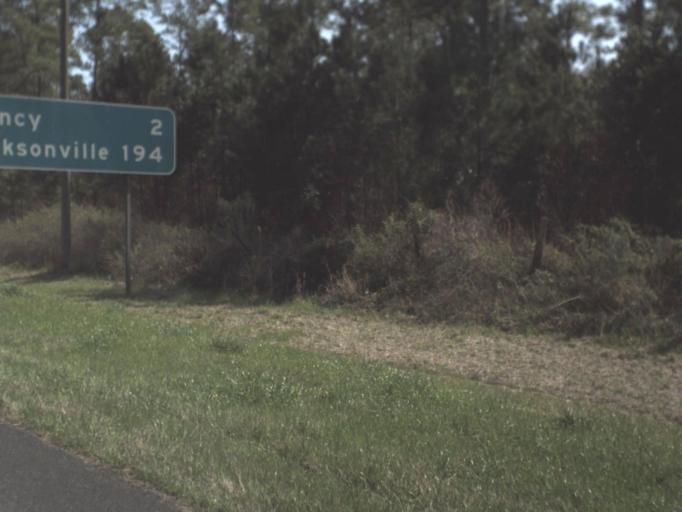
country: US
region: Florida
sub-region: Gadsden County
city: Gretna
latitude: 30.5908
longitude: -84.6395
